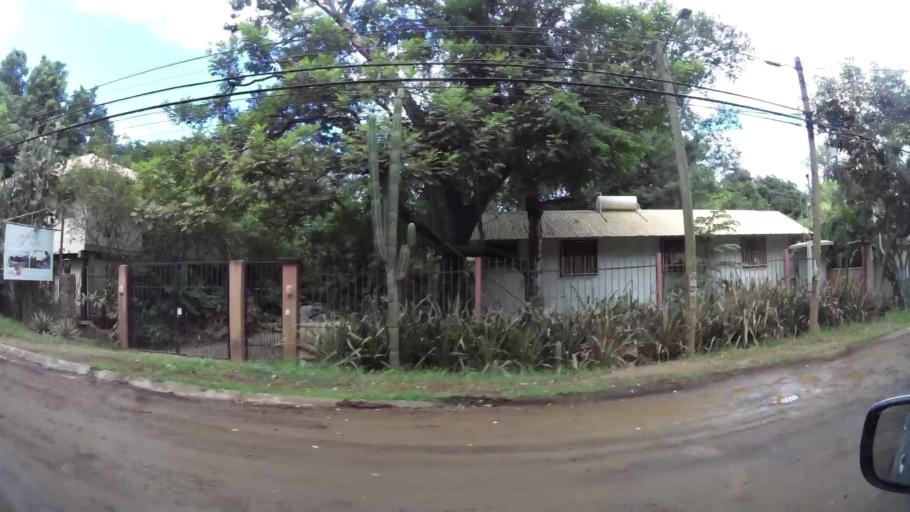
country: CR
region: Guanacaste
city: Santa Cruz
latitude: 10.2939
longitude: -85.8474
